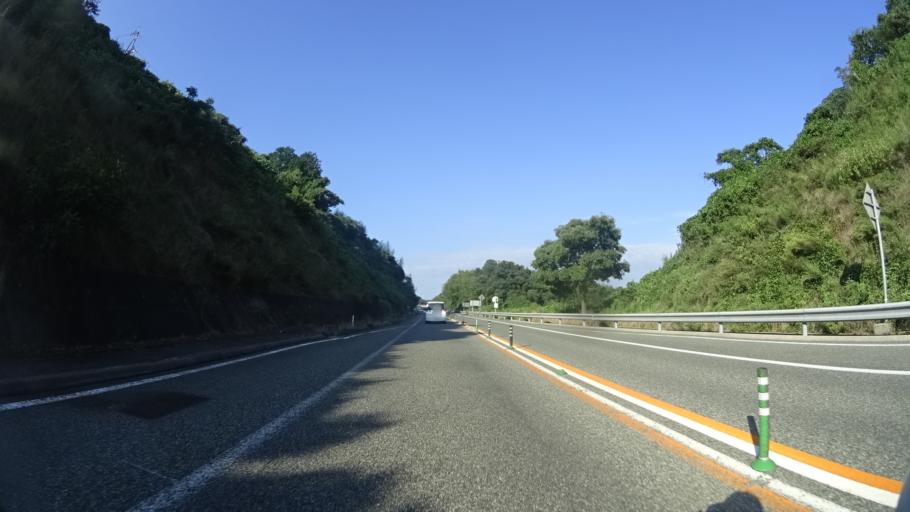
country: JP
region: Shimane
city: Matsue-shi
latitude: 35.4181
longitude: 132.9904
